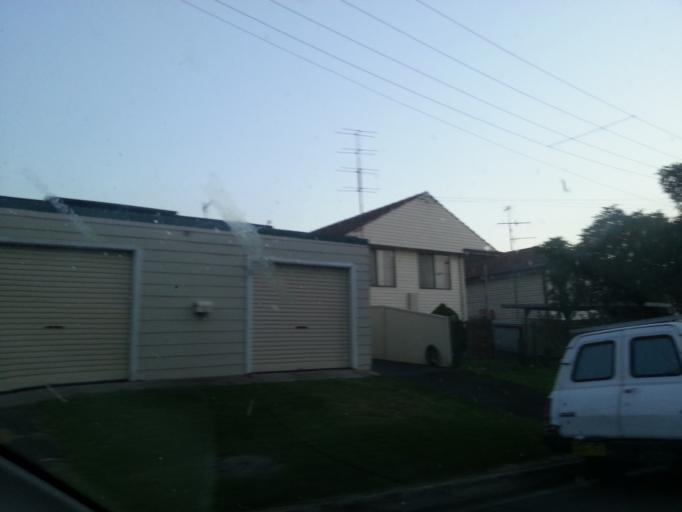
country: AU
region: New South Wales
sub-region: Wollongong
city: Cringila
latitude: -34.4720
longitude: 150.8743
